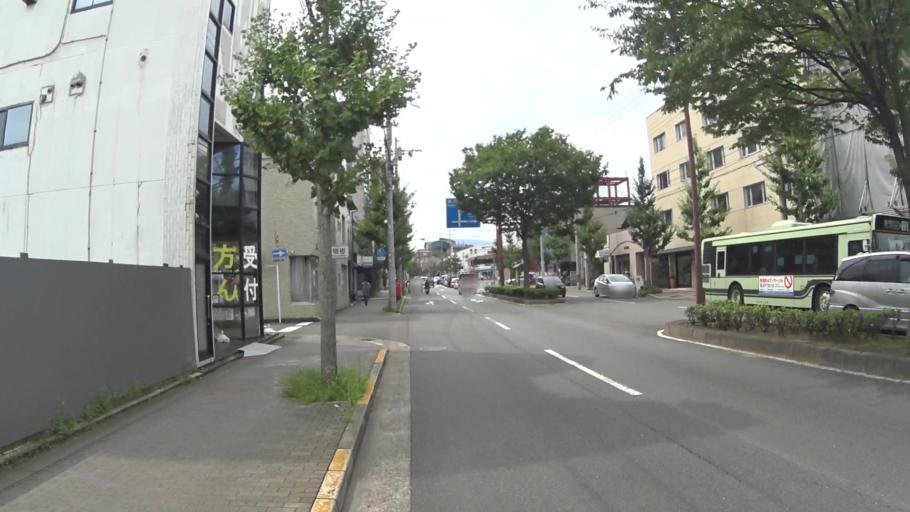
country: JP
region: Kyoto
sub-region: Kyoto-shi
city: Kamigyo-ku
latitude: 35.0514
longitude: 135.7687
